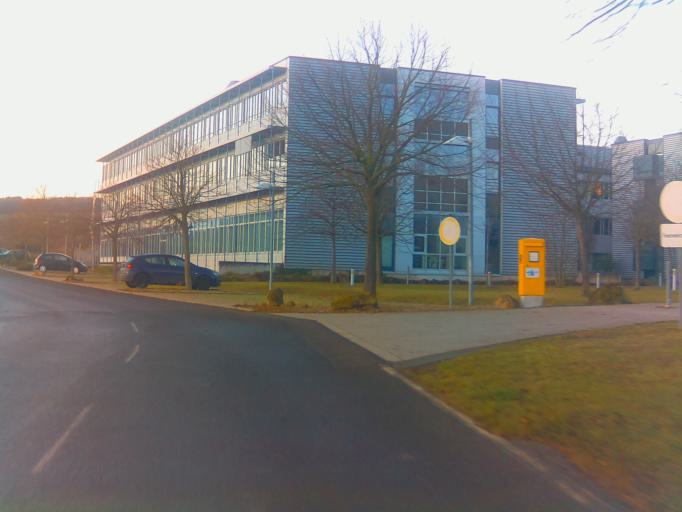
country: DE
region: Rheinland-Pfalz
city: Wendelsheim
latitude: 49.7589
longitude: 7.9849
